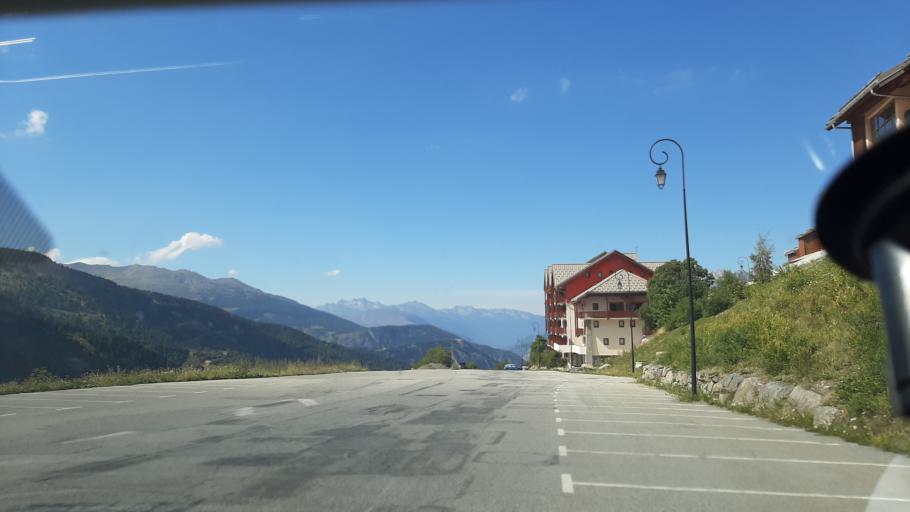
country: FR
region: Rhone-Alpes
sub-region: Departement de la Savoie
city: Saint-Michel-de-Maurienne
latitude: 45.1710
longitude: 6.4952
